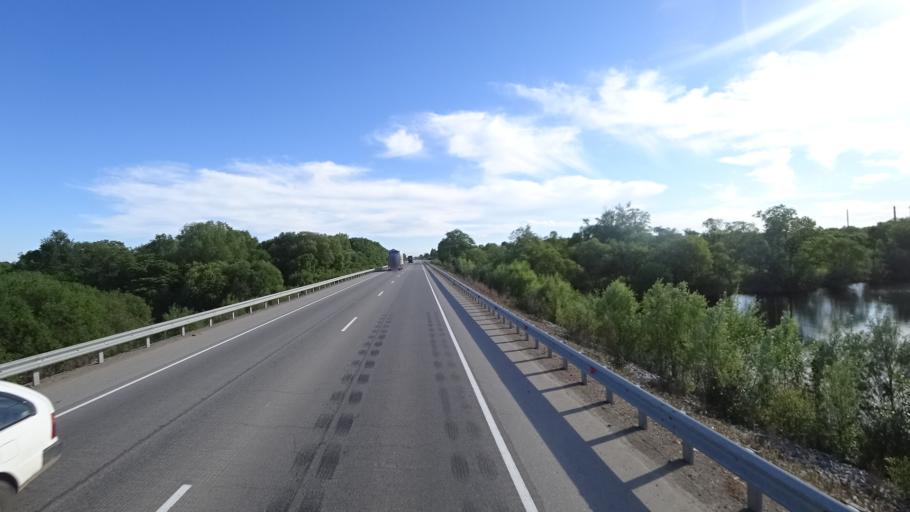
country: RU
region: Khabarovsk Krai
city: Khor
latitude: 47.8779
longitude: 134.9690
